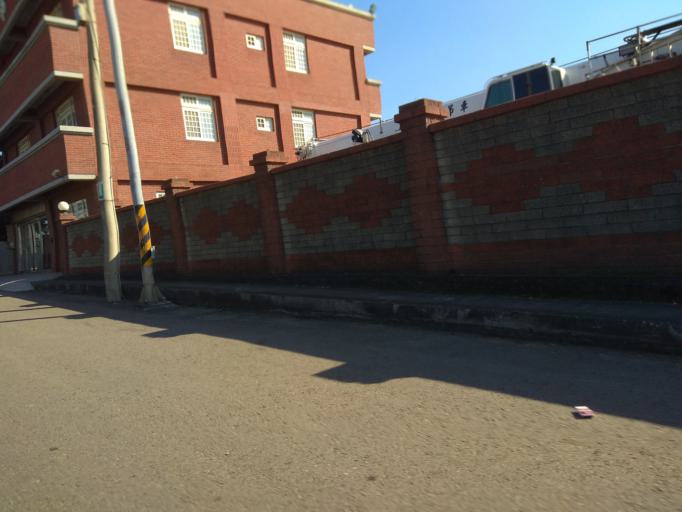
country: TW
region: Taiwan
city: Taoyuan City
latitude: 25.0347
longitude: 121.1019
